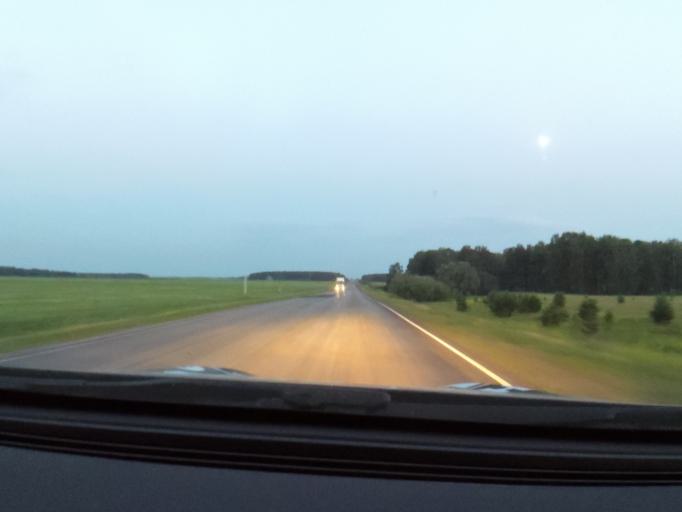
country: RU
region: Bashkortostan
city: Duvan
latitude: 56.0996
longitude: 58.0652
